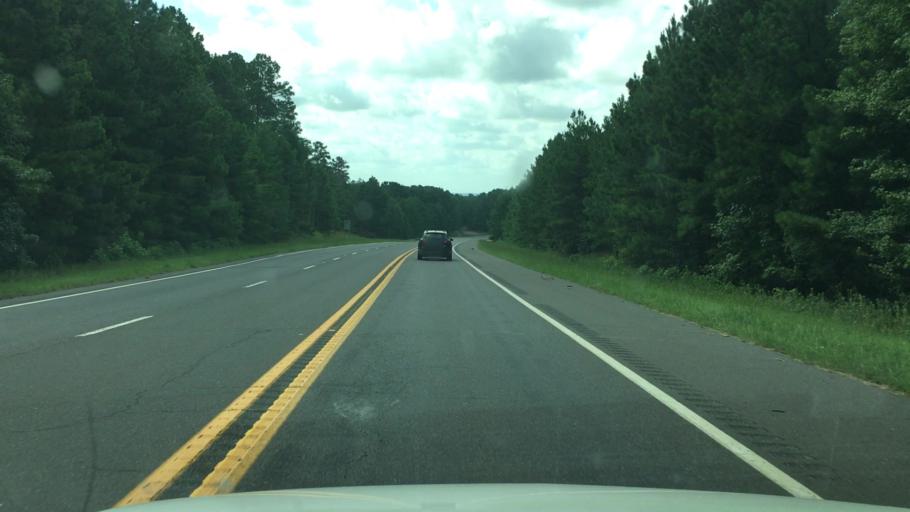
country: US
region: Arkansas
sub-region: Clark County
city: Arkadelphia
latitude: 34.2126
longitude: -93.0821
